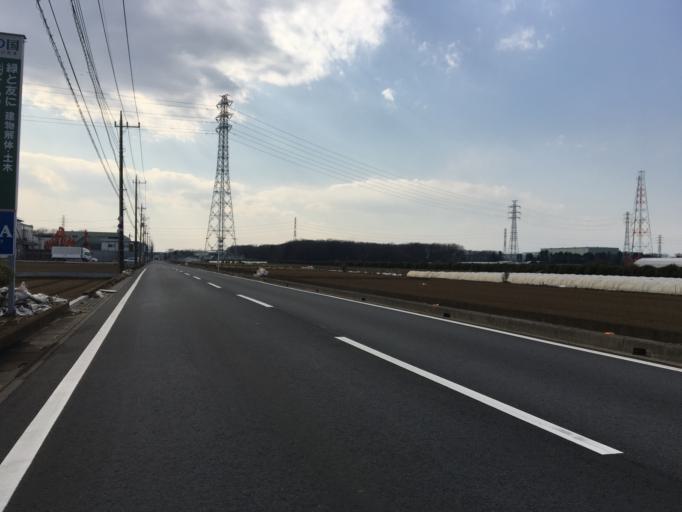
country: JP
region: Saitama
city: Oi
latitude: 35.8207
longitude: 139.5101
